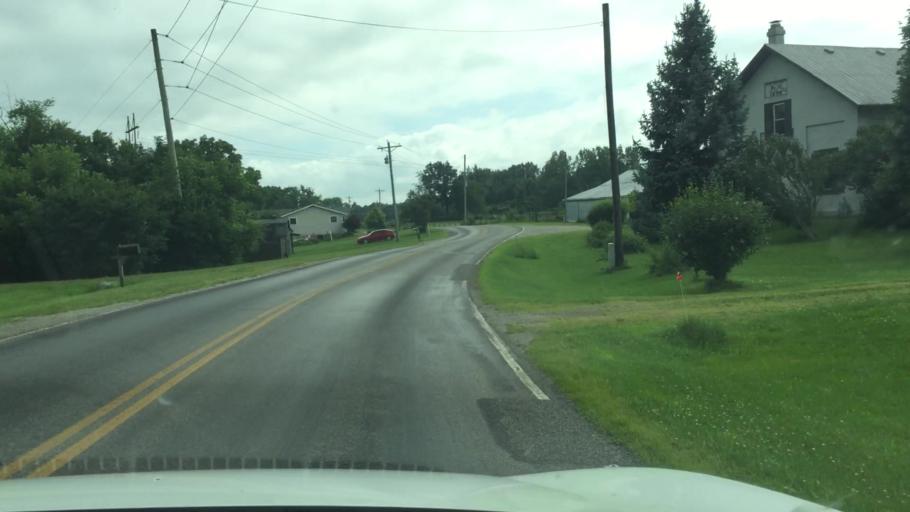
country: US
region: Ohio
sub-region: Champaign County
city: Mechanicsburg
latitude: 40.0583
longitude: -83.6394
